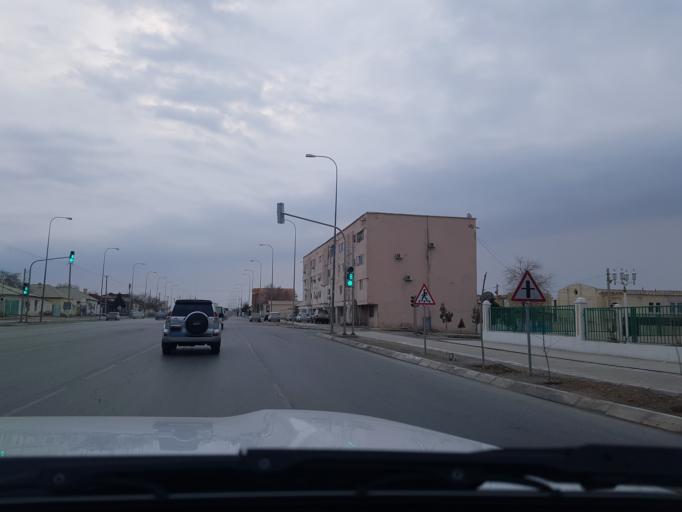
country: TM
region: Balkan
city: Balkanabat
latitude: 39.5153
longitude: 54.3713
